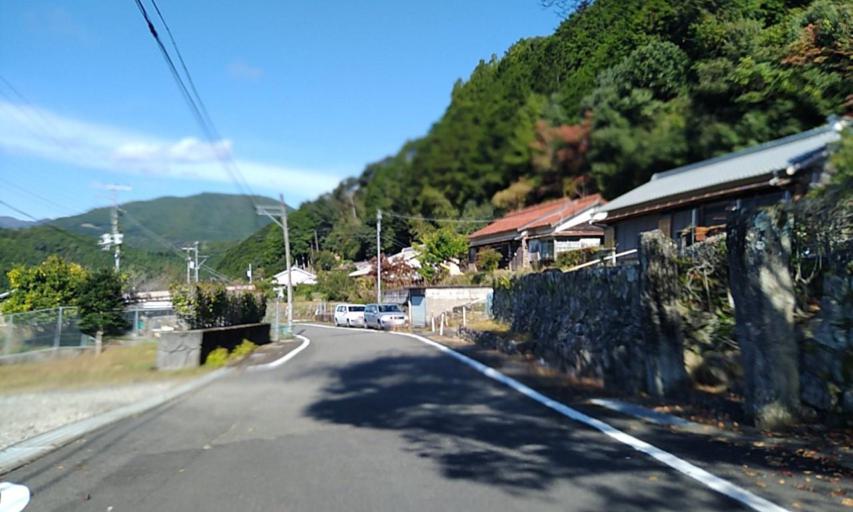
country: JP
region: Wakayama
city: Shingu
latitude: 33.9257
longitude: 135.9829
